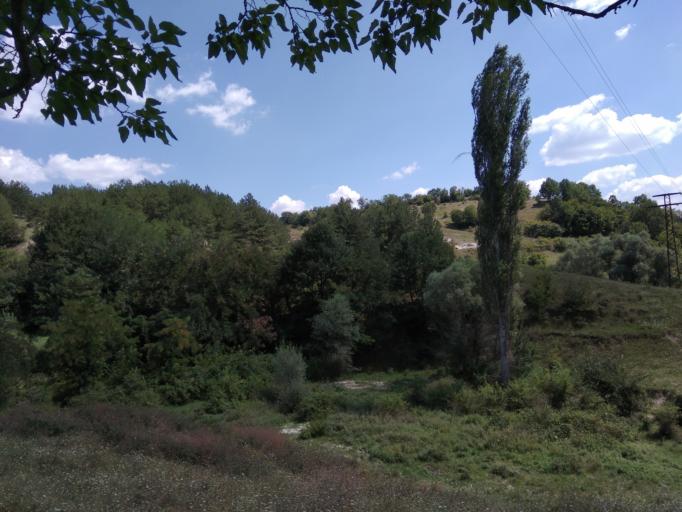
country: BG
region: Kurdzhali
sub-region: Obshtina Kurdzhali
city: Kurdzhali
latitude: 41.6545
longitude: 25.3989
